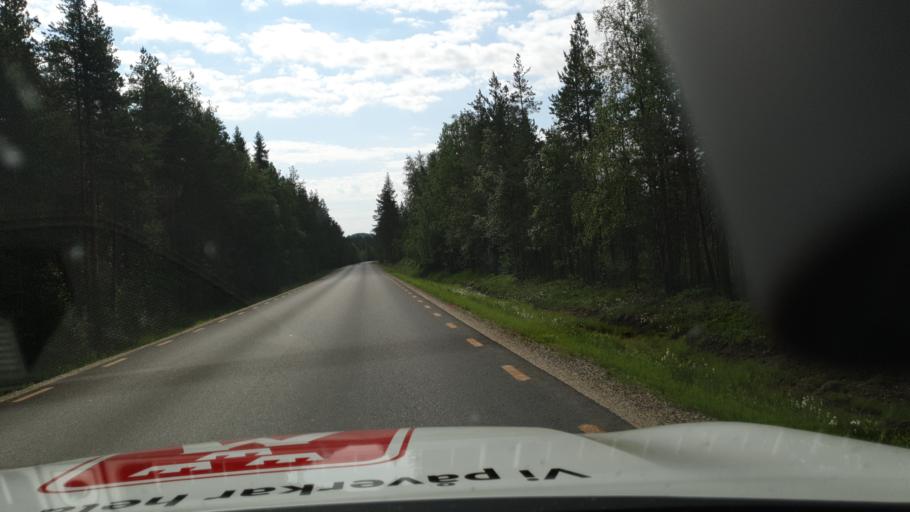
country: SE
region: Vaesterbotten
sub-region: Norsjo Kommun
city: Norsjoe
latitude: 64.4739
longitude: 19.3248
